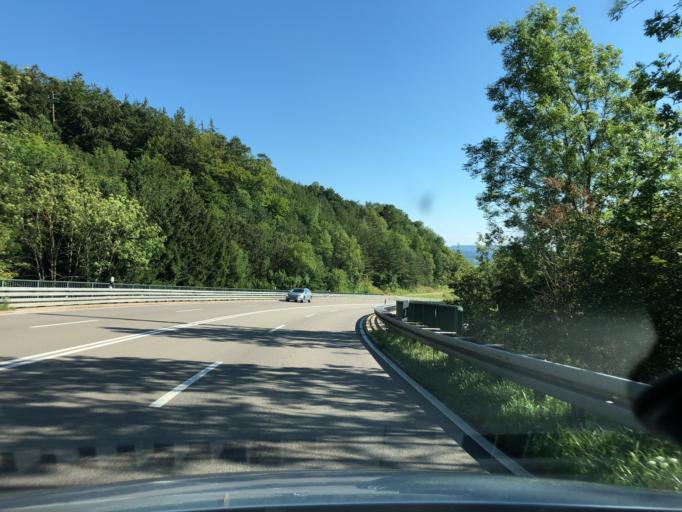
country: DE
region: Baden-Wuerttemberg
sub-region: Freiburg Region
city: Dogern
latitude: 47.6351
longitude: 8.1844
